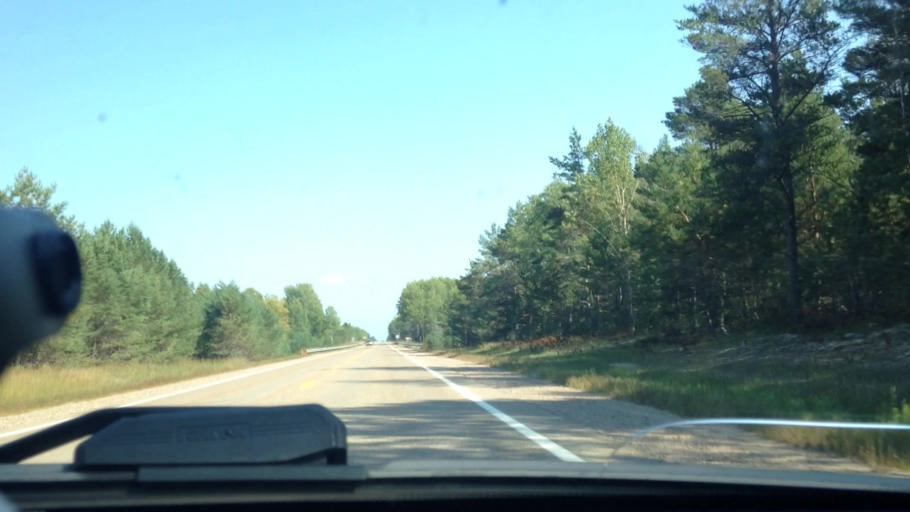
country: US
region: Michigan
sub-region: Mackinac County
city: Saint Ignace
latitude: 46.3584
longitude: -84.8693
